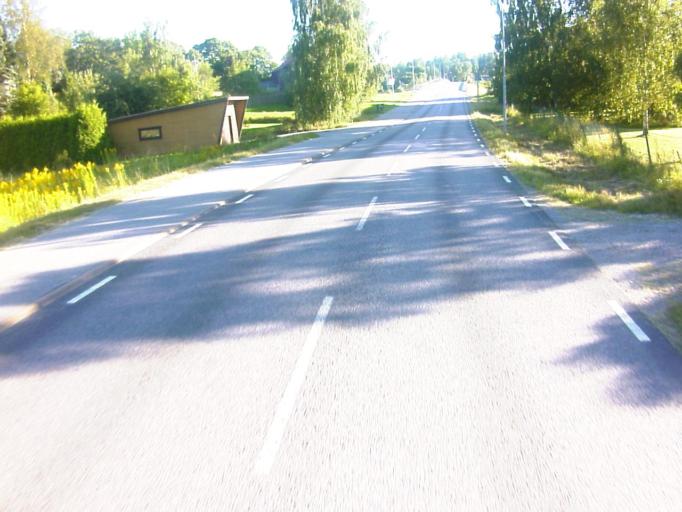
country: SE
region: Soedermanland
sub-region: Eskilstuna Kommun
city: Hallbybrunn
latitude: 59.3949
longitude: 16.4350
